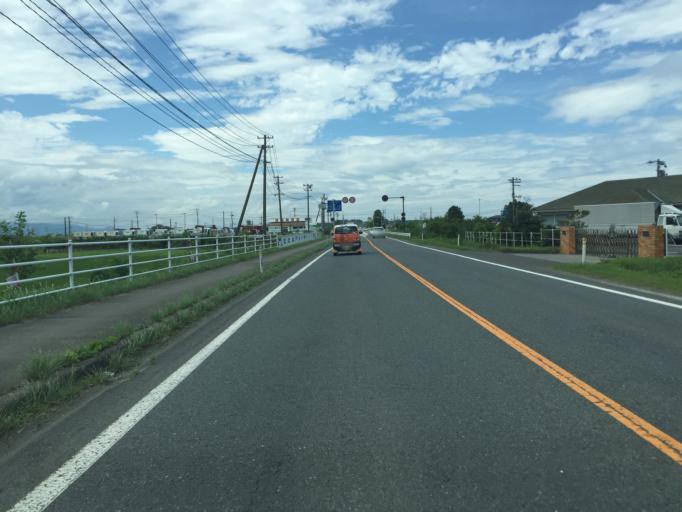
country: JP
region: Fukushima
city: Namie
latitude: 37.6916
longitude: 140.9756
